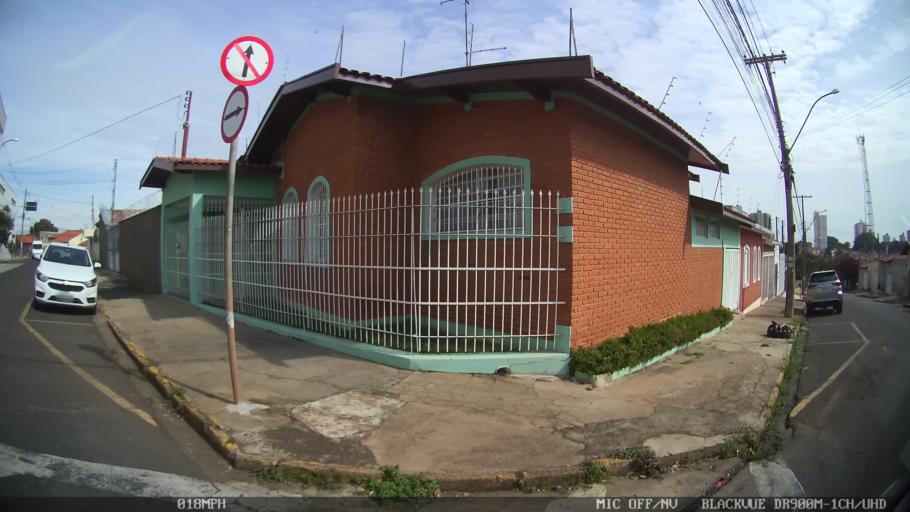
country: BR
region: Sao Paulo
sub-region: Piracicaba
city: Piracicaba
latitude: -22.7412
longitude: -47.6506
